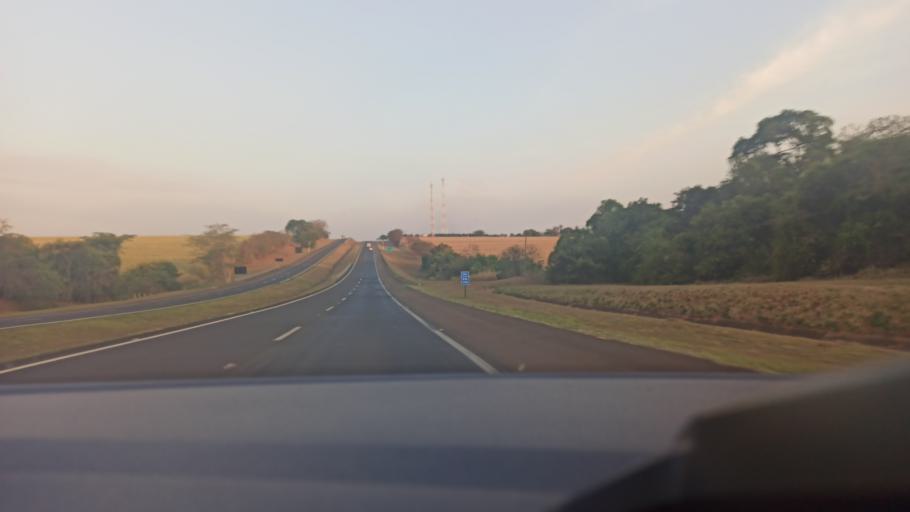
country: BR
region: Sao Paulo
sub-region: Taquaritinga
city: Taquaritinga
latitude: -21.4182
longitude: -48.6817
